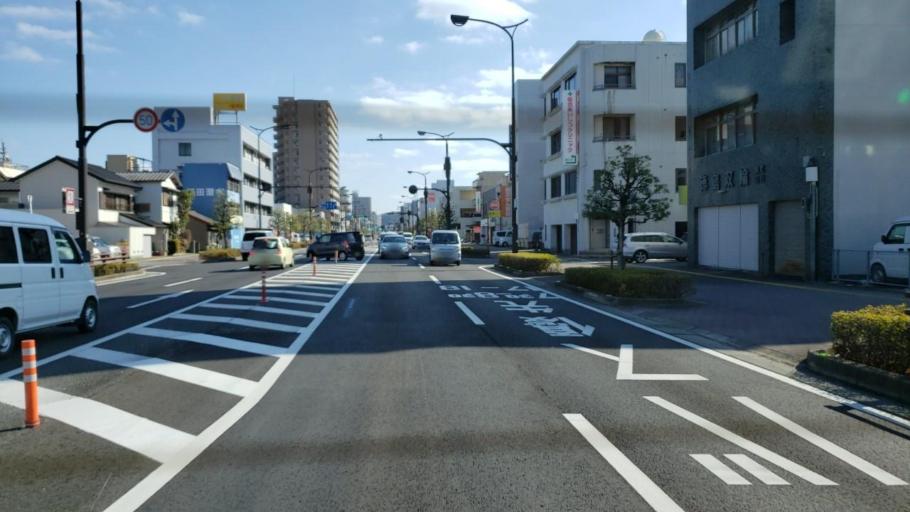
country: JP
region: Tokushima
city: Tokushima-shi
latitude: 34.0786
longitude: 134.5317
